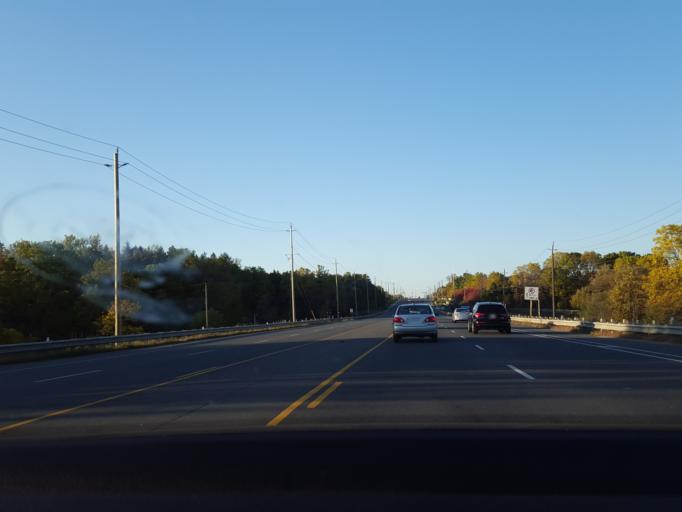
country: CA
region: Ontario
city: Newmarket
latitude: 44.0207
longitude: -79.4725
